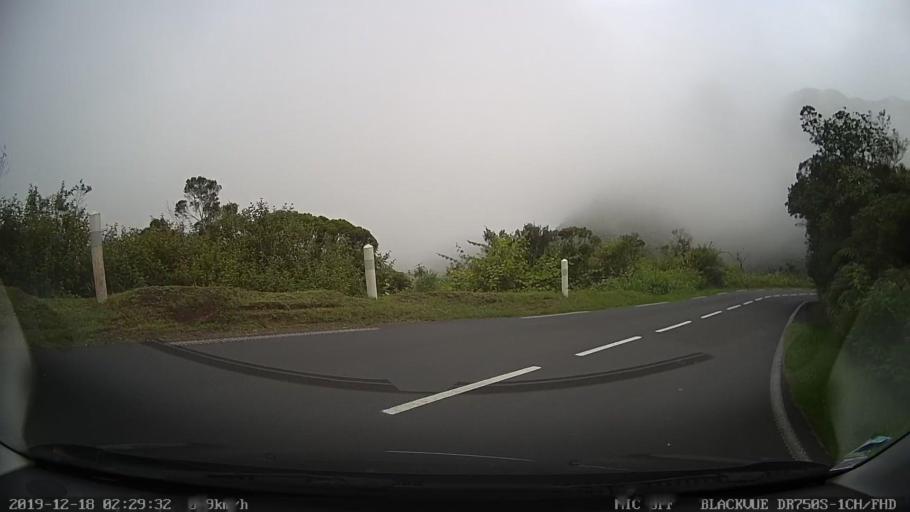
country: RE
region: Reunion
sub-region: Reunion
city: Cilaos
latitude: -21.1564
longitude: 55.5995
